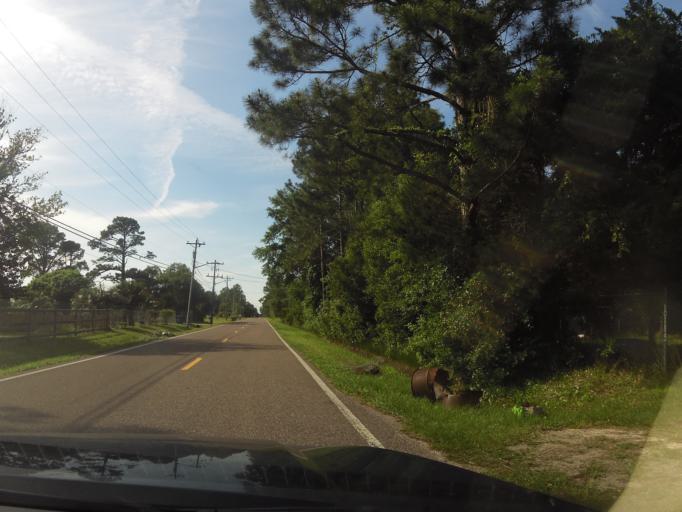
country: US
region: Florida
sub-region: Nassau County
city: Fernandina Beach
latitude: 30.5119
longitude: -81.4767
